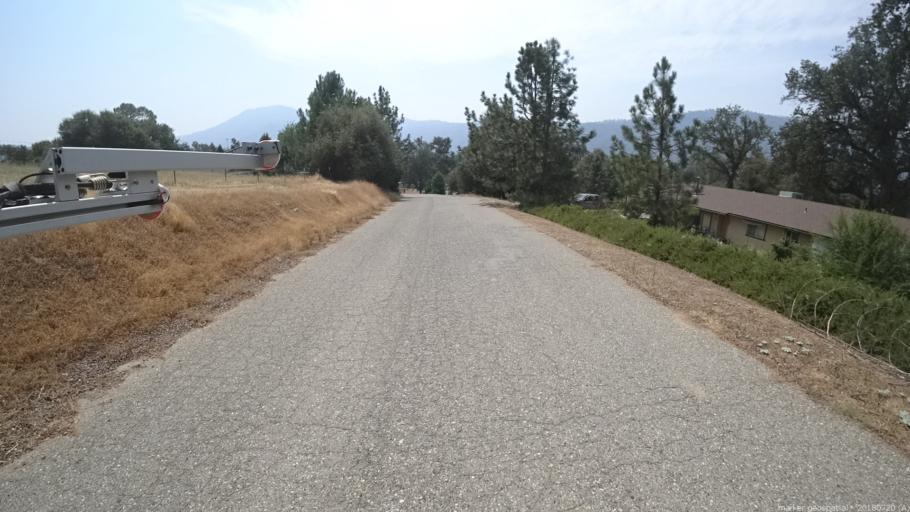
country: US
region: California
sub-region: Madera County
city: Ahwahnee
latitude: 37.3538
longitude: -119.7226
